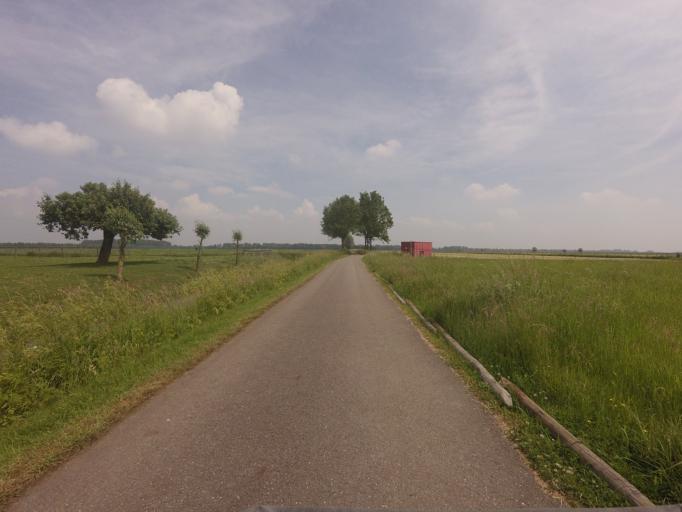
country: NL
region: Utrecht
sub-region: Gemeente Houten
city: Houten
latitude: 51.9919
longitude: 5.1961
